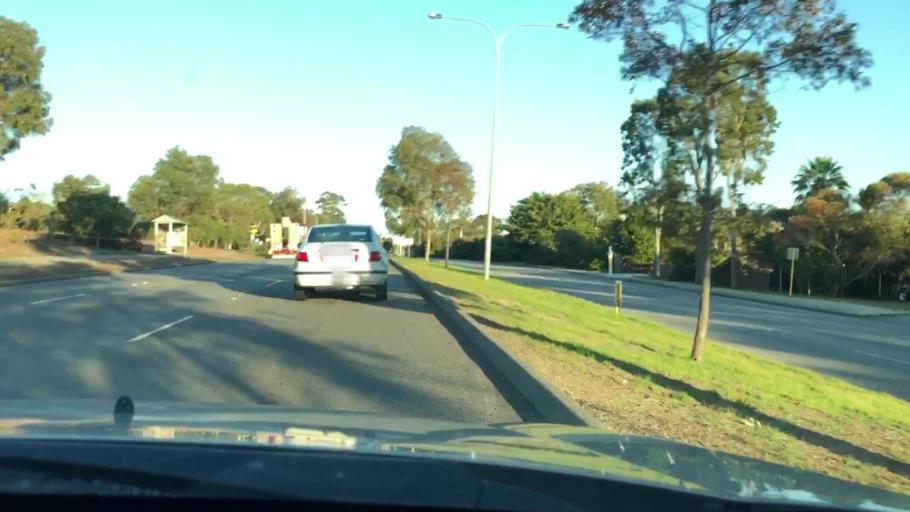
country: AU
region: Western Australia
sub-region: Melville
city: Booragoon
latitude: -32.0460
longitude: 115.8405
